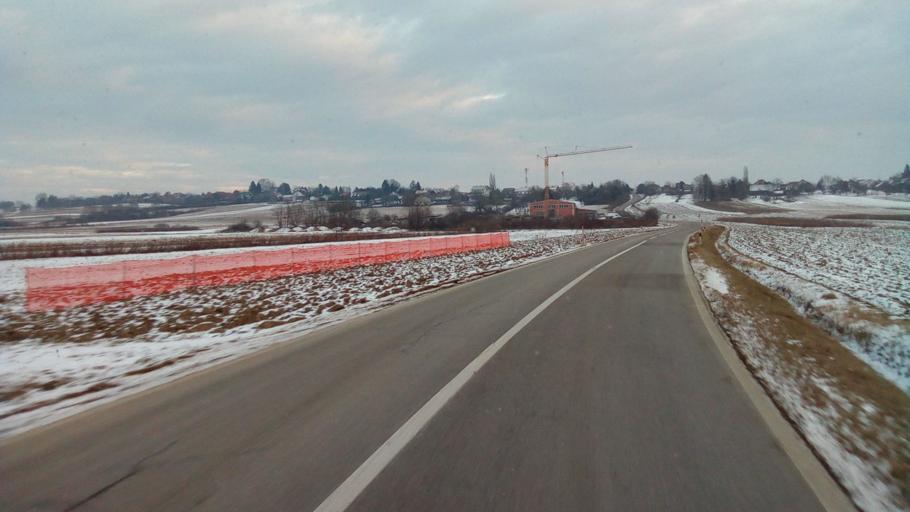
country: HR
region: Koprivnicko-Krizevacka
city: Krizevci
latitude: 45.9867
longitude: 16.4673
